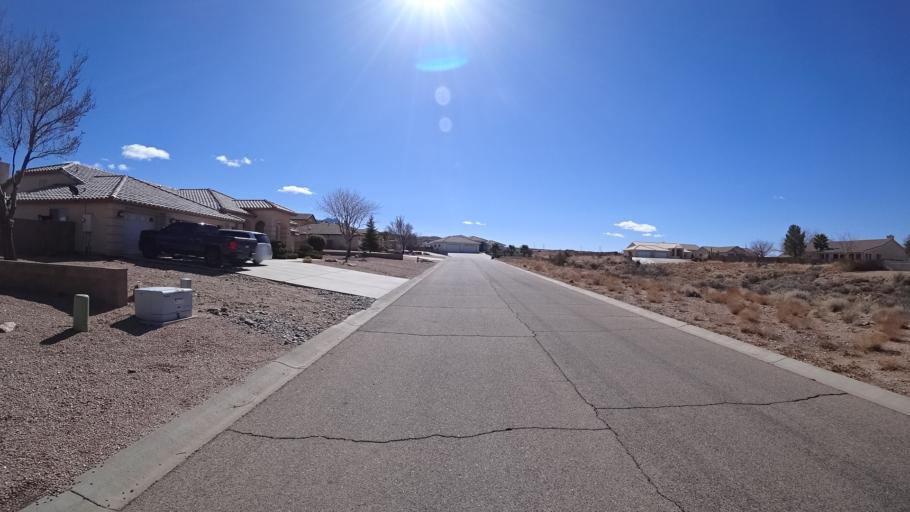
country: US
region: Arizona
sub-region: Mohave County
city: Kingman
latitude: 35.1985
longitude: -113.9593
